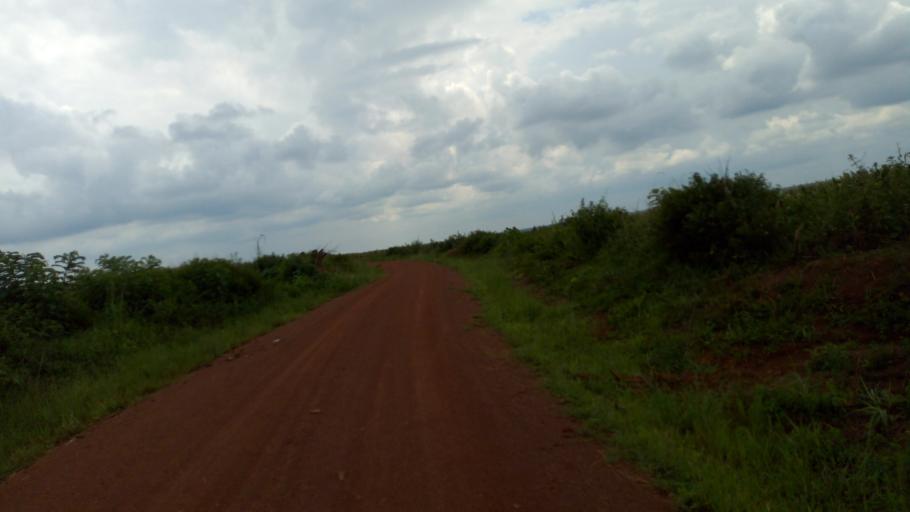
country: UG
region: Western Region
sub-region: Masindi District
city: Masindi
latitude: 1.5429
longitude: 31.7512
